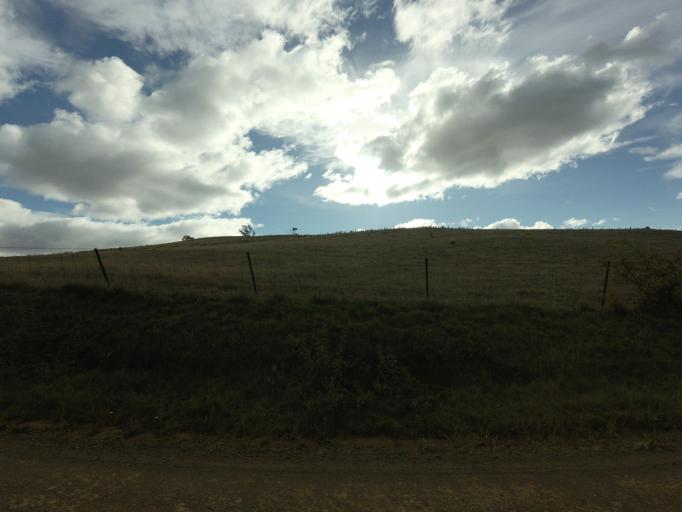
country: AU
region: Tasmania
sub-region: Brighton
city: Bridgewater
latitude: -42.4605
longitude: 147.2764
